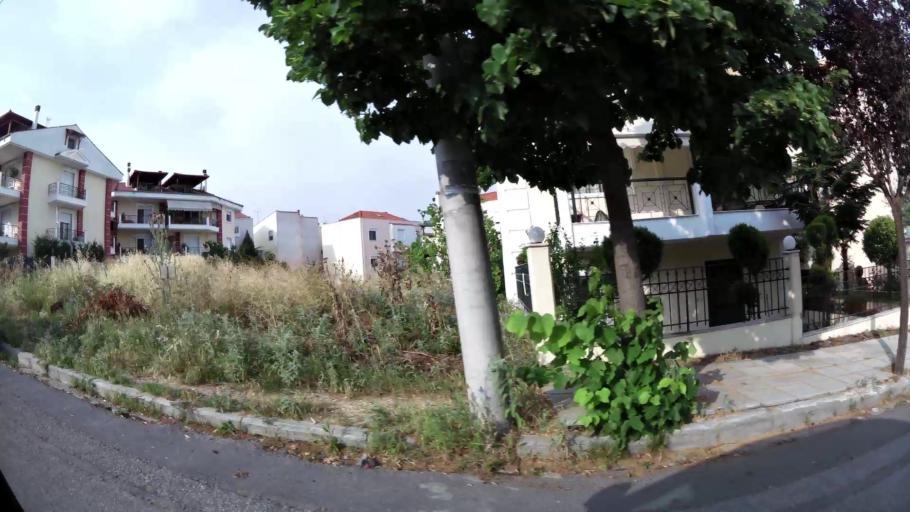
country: GR
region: Central Macedonia
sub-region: Nomos Thessalonikis
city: Oraiokastro
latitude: 40.7217
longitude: 22.9181
